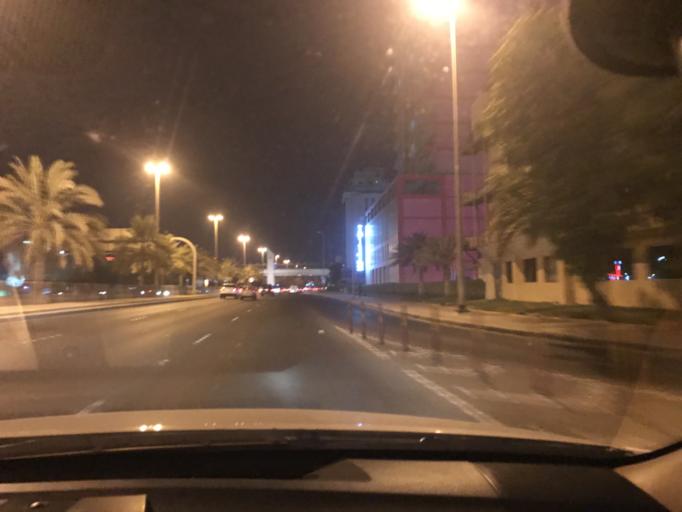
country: BH
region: Manama
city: Manama
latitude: 26.2342
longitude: 50.5980
